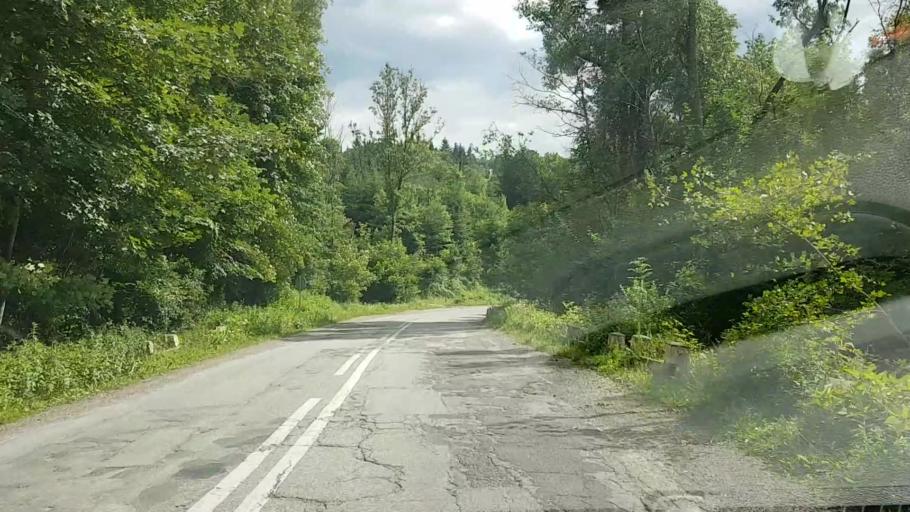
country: RO
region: Neamt
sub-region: Comuna Poiana Teiului
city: Poiana Teiului
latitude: 47.0830
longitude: 25.9698
